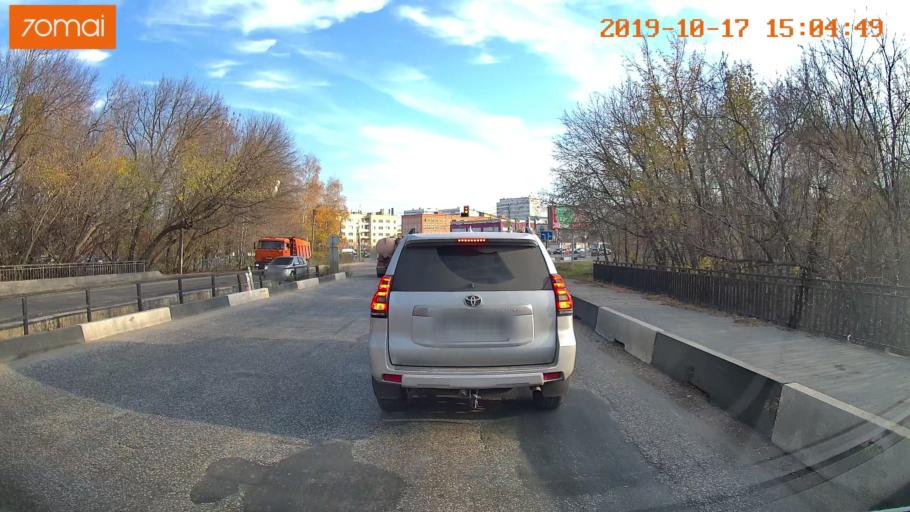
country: RU
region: Rjazan
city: Ryazan'
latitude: 54.6377
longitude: 39.7220
